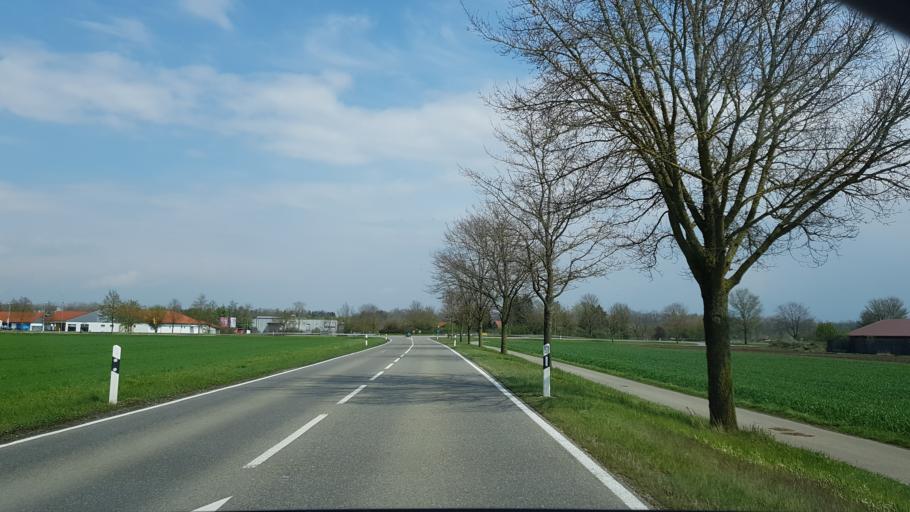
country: DE
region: Baden-Wuerttemberg
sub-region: Tuebingen Region
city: Dietenheim
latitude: 48.2025
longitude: 10.0703
